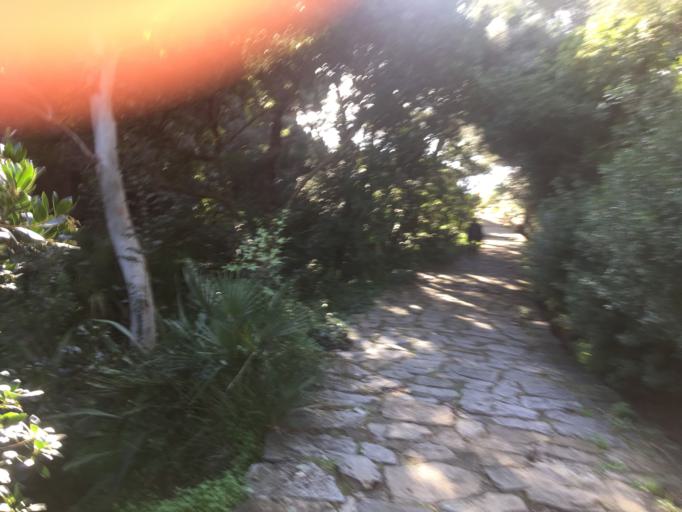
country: FR
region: Provence-Alpes-Cote d'Azur
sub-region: Departement du Var
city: Cavalaire-sur-Mer
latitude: 43.1547
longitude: 6.4827
